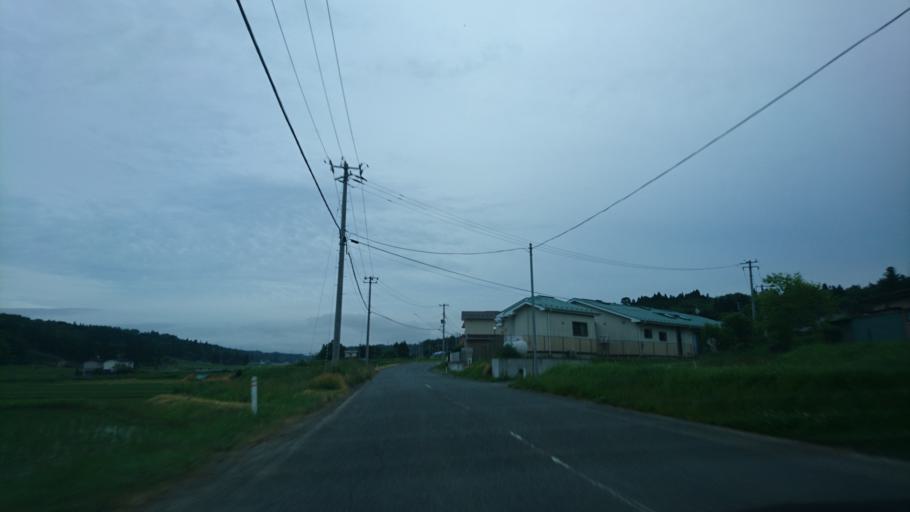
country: JP
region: Iwate
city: Ichinoseki
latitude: 38.9301
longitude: 141.1725
